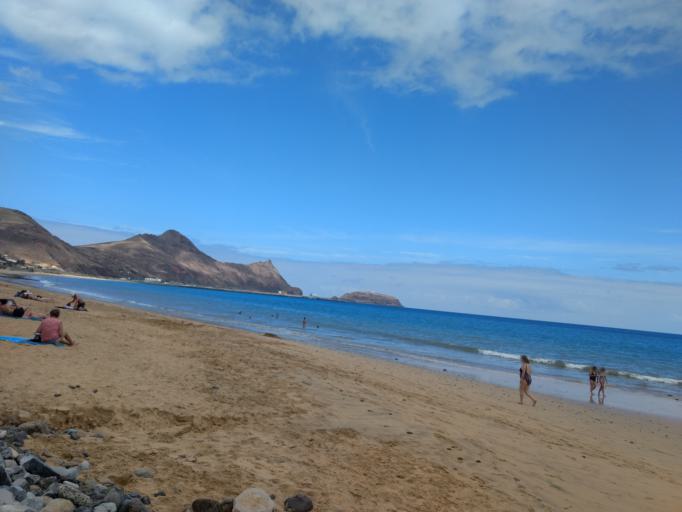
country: PT
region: Madeira
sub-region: Porto Santo
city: Vila de Porto Santo
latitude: 33.0584
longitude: -16.3330
